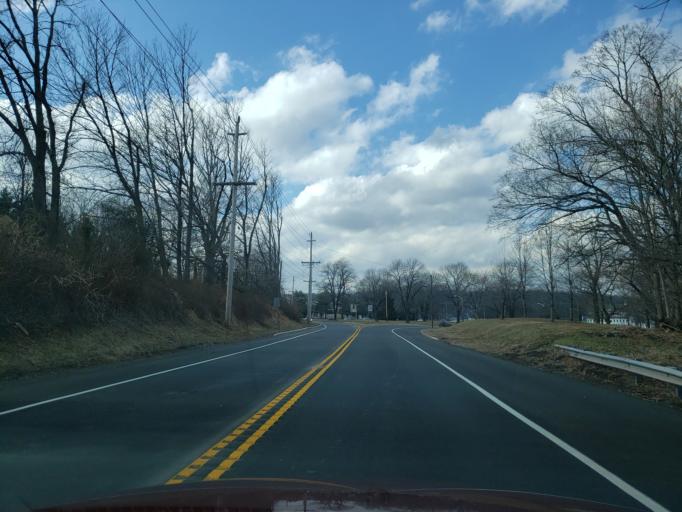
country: US
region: New Jersey
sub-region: Hunterdon County
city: Flemington
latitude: 40.5035
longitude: -74.8689
